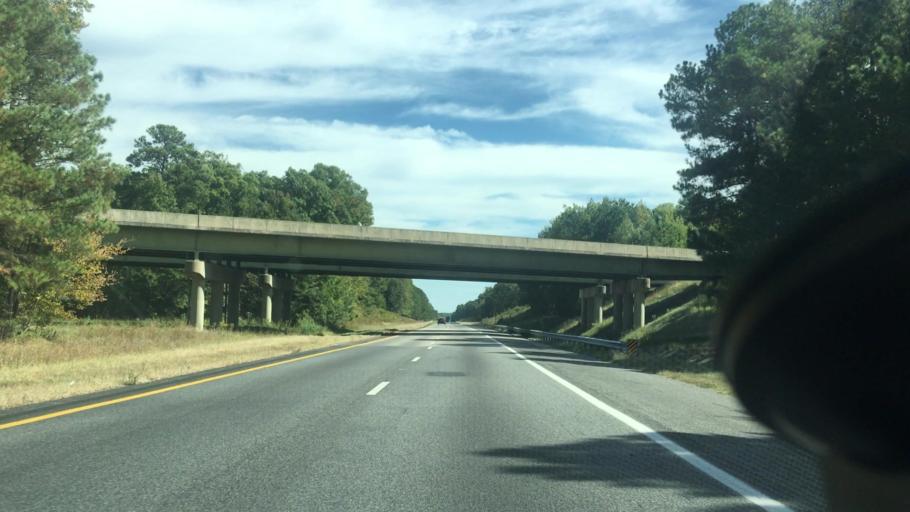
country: US
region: Virginia
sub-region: Chesterfield County
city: Chesterfield
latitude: 37.4087
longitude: -77.5664
